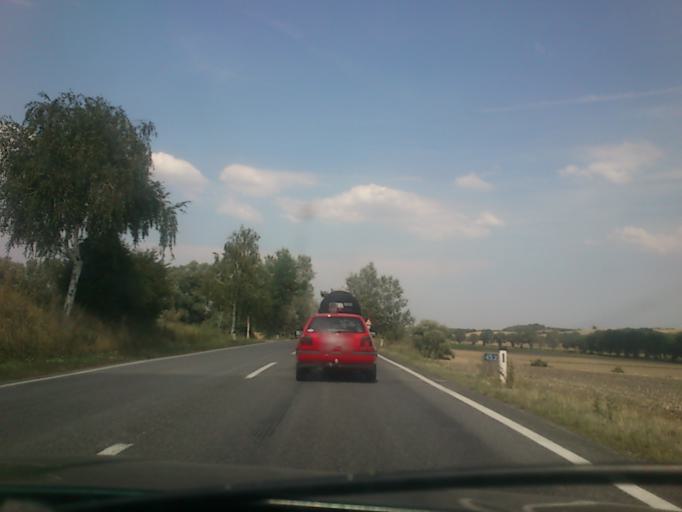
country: AT
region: Lower Austria
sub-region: Politischer Bezirk Mistelbach
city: Wilfersdorf
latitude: 48.6115
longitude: 16.6481
